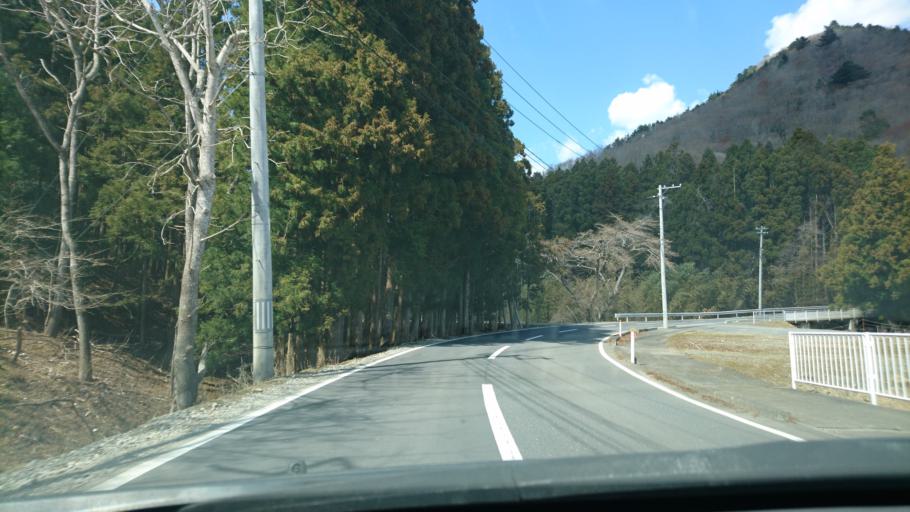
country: JP
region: Miyagi
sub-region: Oshika Gun
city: Onagawa Cho
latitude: 38.4689
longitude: 141.4720
